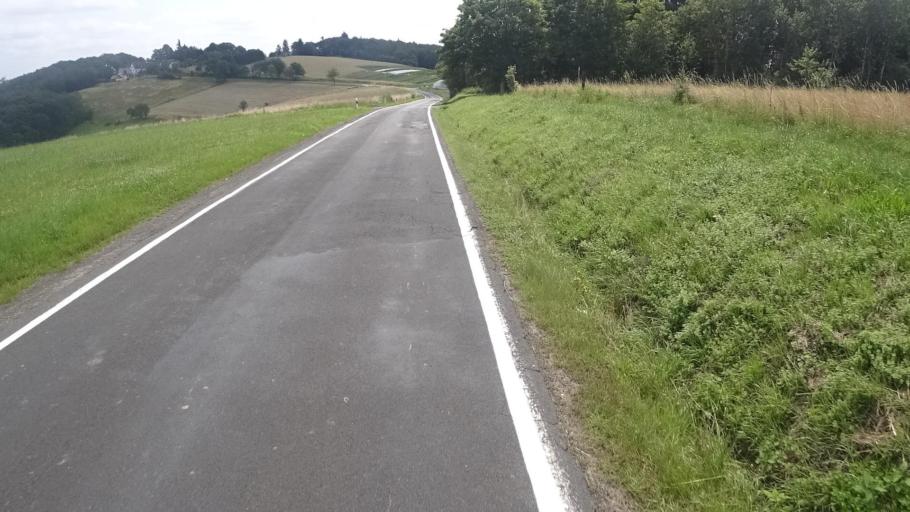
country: DE
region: Rheinland-Pfalz
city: Sankt Katharinen
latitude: 50.5866
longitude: 7.3579
